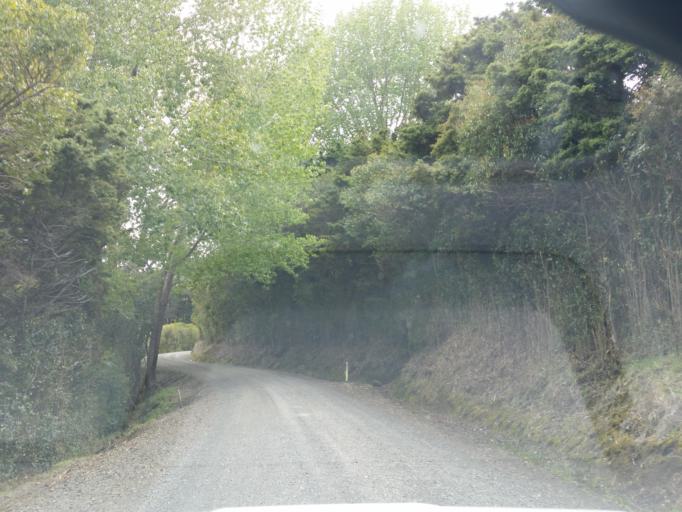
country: NZ
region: Northland
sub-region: Whangarei
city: Maungatapere
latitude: -35.9015
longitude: 174.1166
